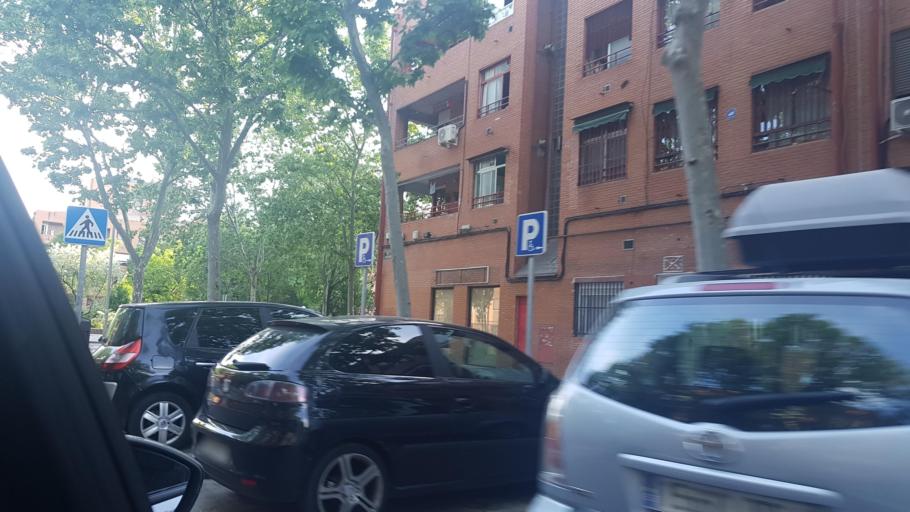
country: ES
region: Madrid
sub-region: Provincia de Madrid
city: Puente de Vallecas
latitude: 40.3734
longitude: -3.6581
